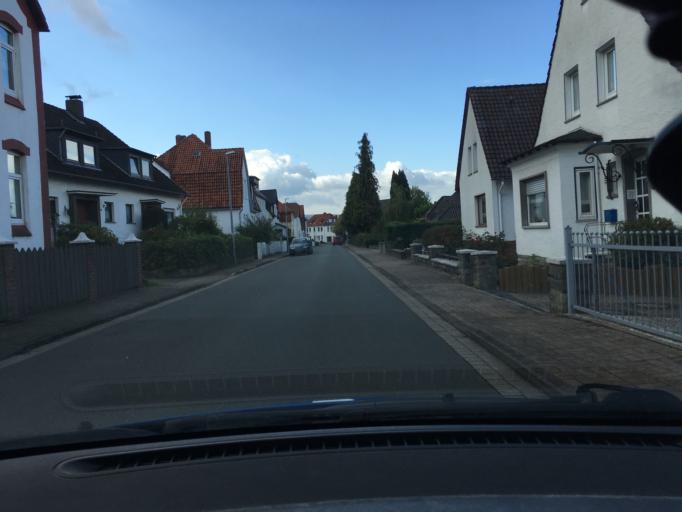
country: DE
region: Lower Saxony
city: Bad Munder am Deister
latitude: 52.1926
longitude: 9.4606
